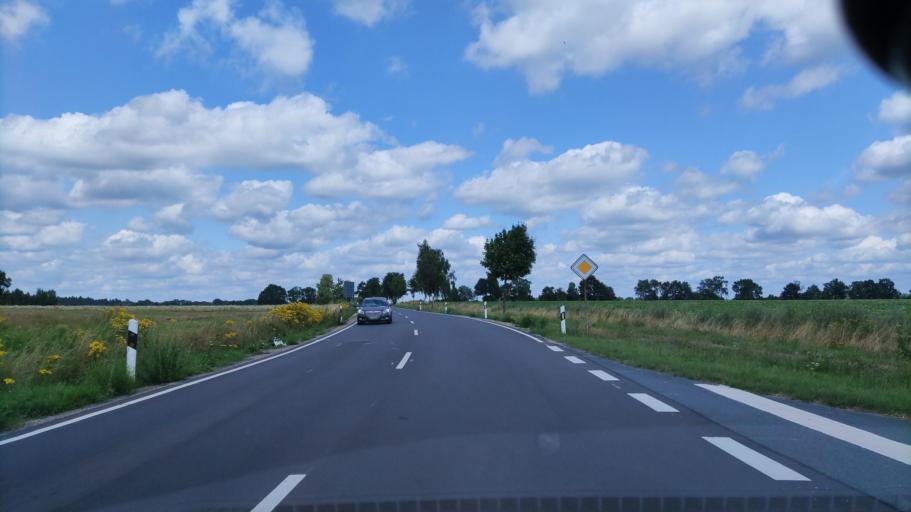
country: DE
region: Lower Saxony
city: Walsrode
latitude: 52.8886
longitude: 9.6057
